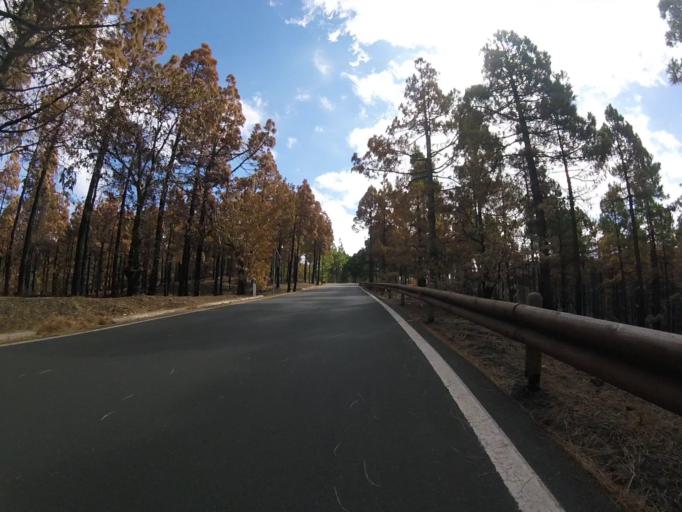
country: ES
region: Canary Islands
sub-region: Provincia de Las Palmas
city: Tejeda
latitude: 27.9736
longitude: -15.5787
